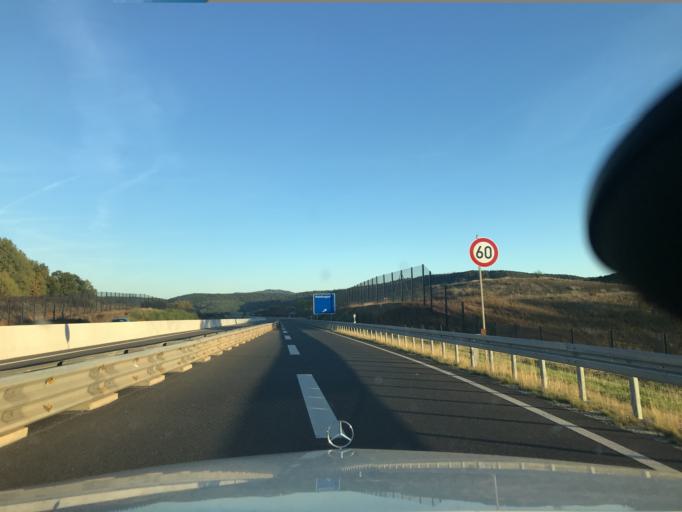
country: DE
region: Hesse
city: Waldkappel
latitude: 51.1482
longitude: 9.9176
